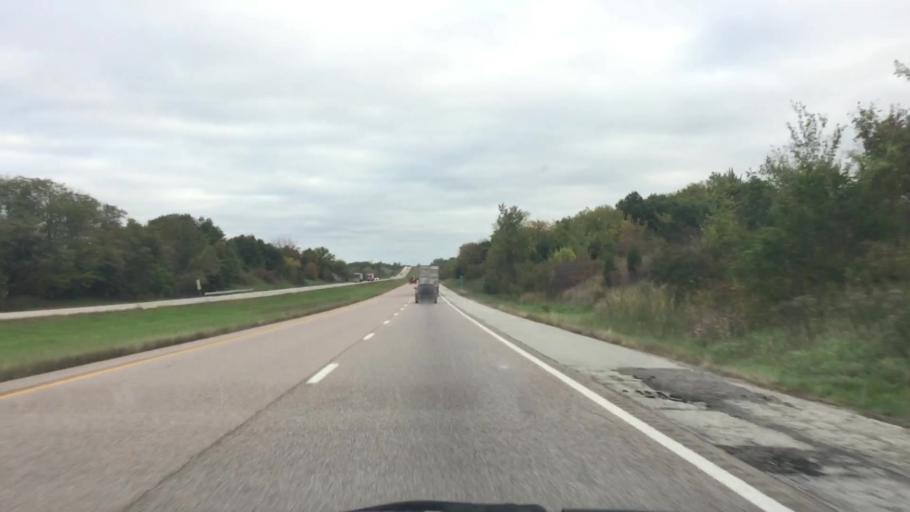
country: US
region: Missouri
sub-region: Clinton County
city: Lathrop
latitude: 39.4993
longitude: -94.2957
